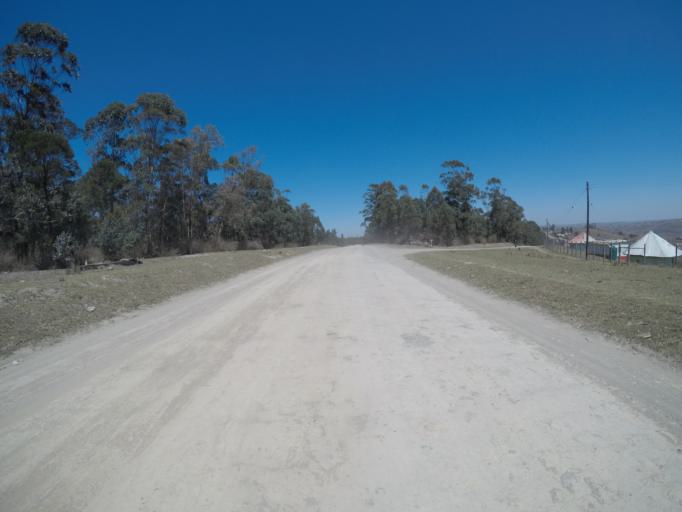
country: ZA
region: Eastern Cape
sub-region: OR Tambo District Municipality
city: Libode
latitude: -31.9491
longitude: 29.0250
